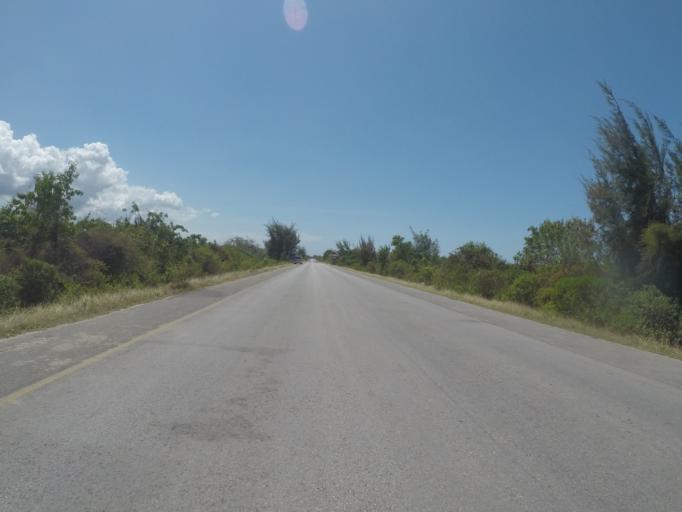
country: TZ
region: Zanzibar Central/South
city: Nganane
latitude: -6.2993
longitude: 39.5383
